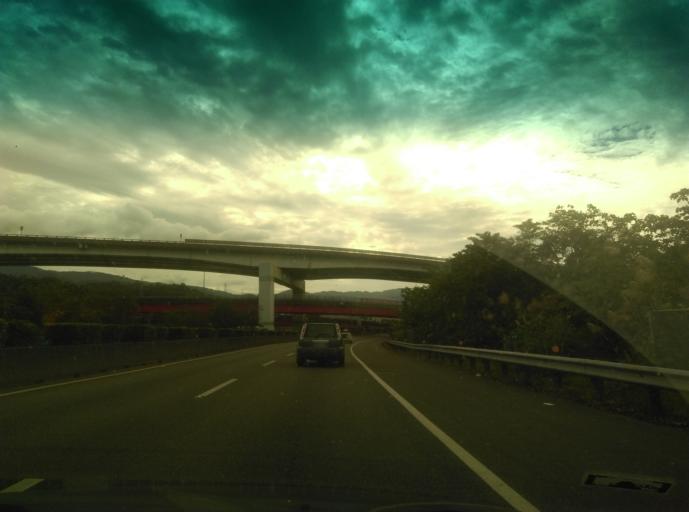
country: TW
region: Taiwan
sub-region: Keelung
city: Keelung
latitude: 25.1066
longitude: 121.7246
